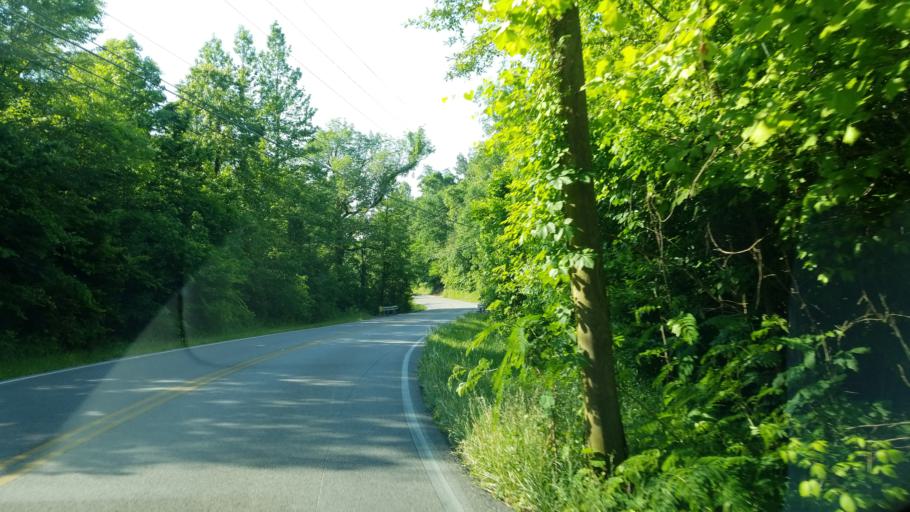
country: US
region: Tennessee
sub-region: Hamilton County
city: Collegedale
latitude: 35.0828
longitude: -85.0094
